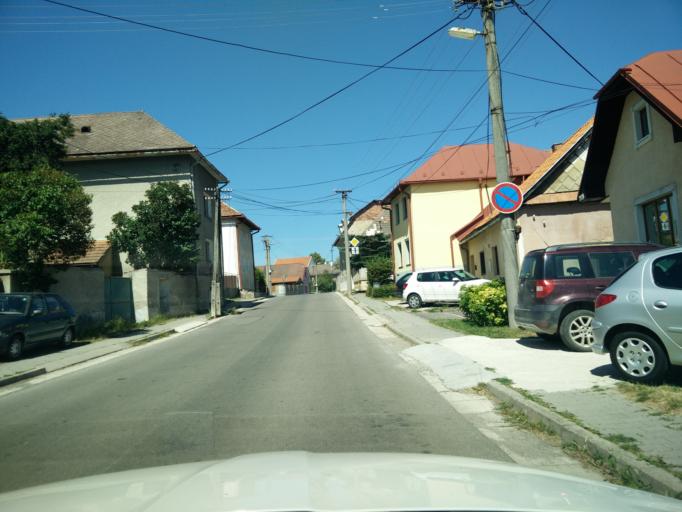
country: SK
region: Nitriansky
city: Prievidza
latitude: 48.8699
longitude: 18.6315
